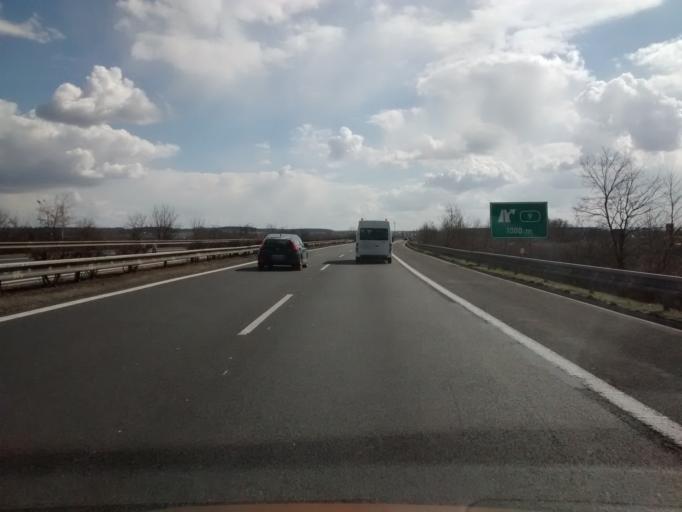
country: CZ
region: Central Bohemia
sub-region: Okres Melnik
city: Veltrusy
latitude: 50.2601
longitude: 14.3694
